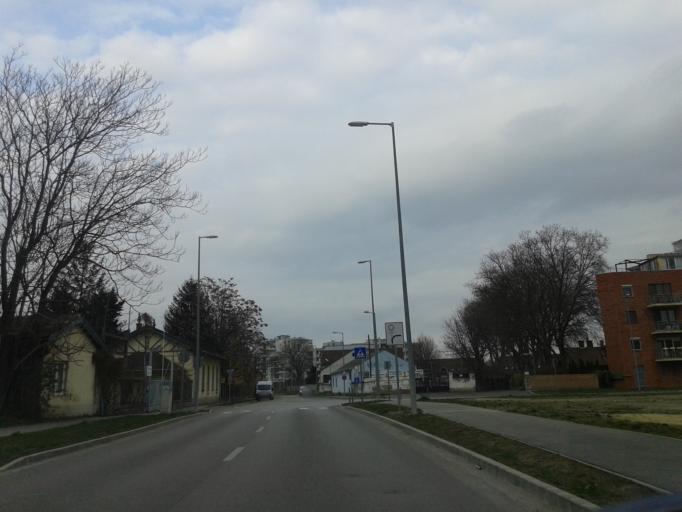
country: HU
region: Gyor-Moson-Sopron
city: Gyor
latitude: 47.6929
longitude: 17.6413
